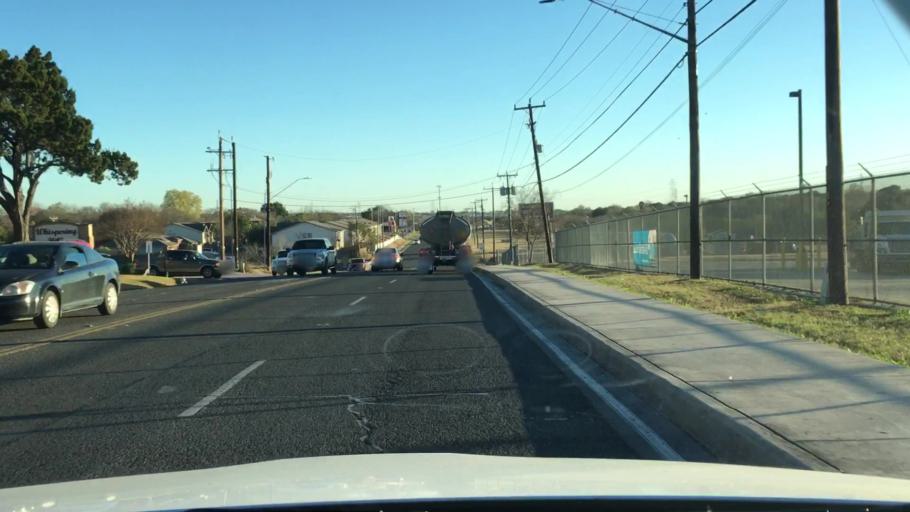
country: US
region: Texas
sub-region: Bexar County
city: Live Oak
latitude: 29.5659
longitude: -98.3836
